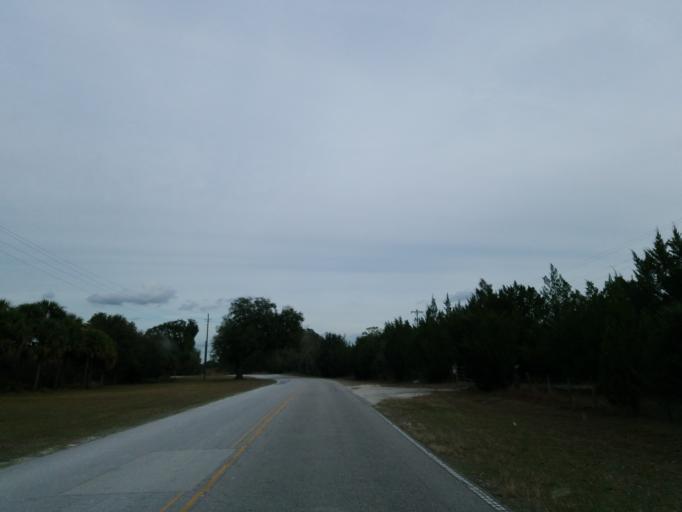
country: US
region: Florida
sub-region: Sumter County
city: Bushnell
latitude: 28.6040
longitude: -82.1686
